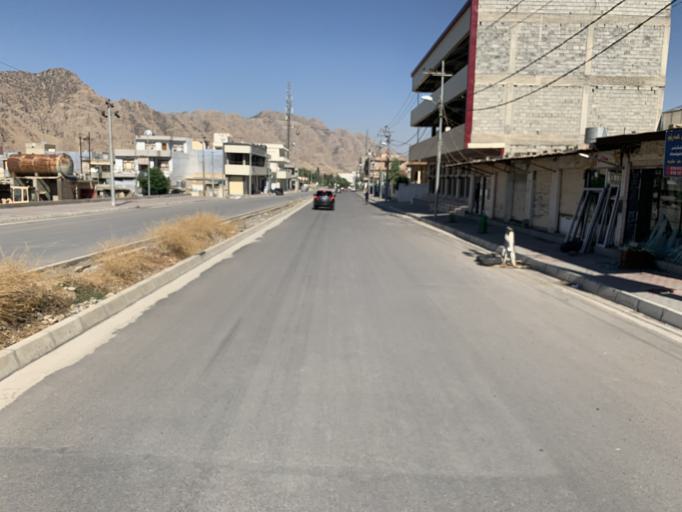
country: IQ
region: As Sulaymaniyah
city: Raniye
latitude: 36.2573
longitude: 44.8740
